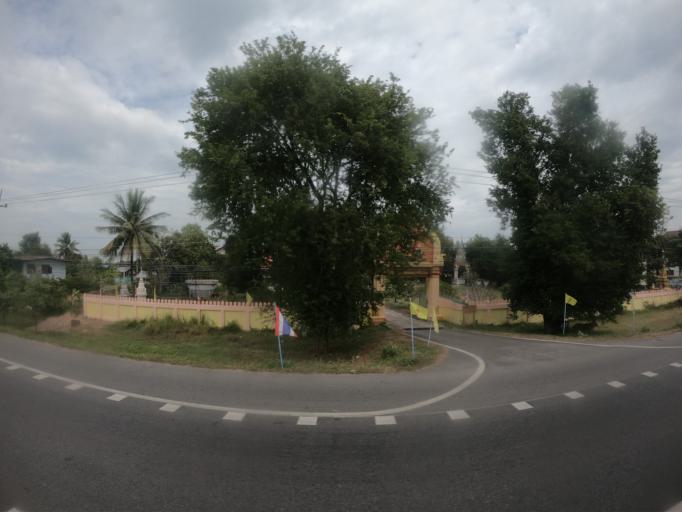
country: TH
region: Maha Sarakham
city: Maha Sarakham
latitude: 16.1547
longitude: 103.3721
